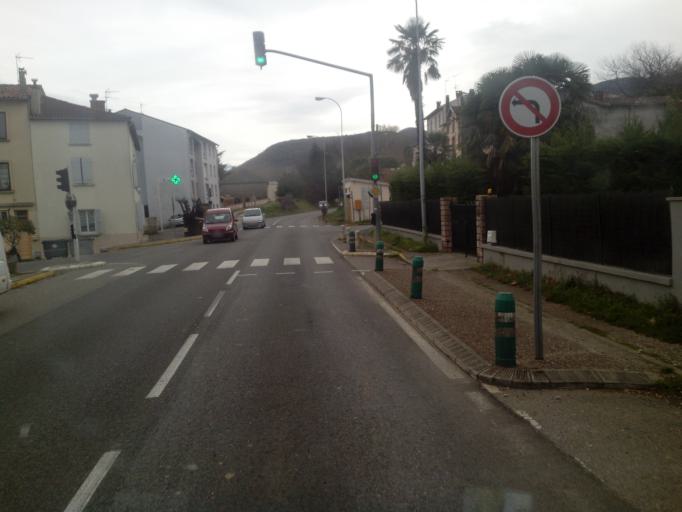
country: FR
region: Midi-Pyrenees
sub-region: Departement de l'Ariege
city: Saint-Girons
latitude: 42.9841
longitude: 1.1413
